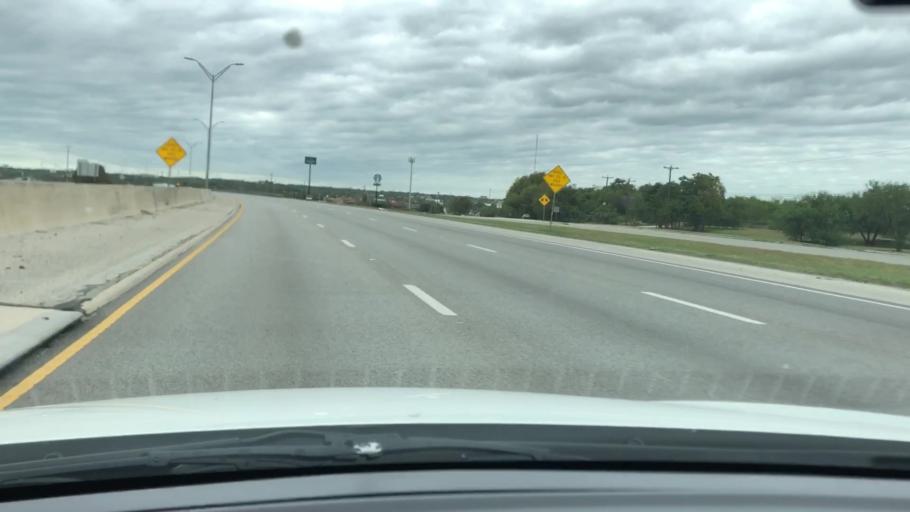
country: US
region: Texas
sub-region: Bexar County
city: Kirby
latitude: 29.4274
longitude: -98.4184
